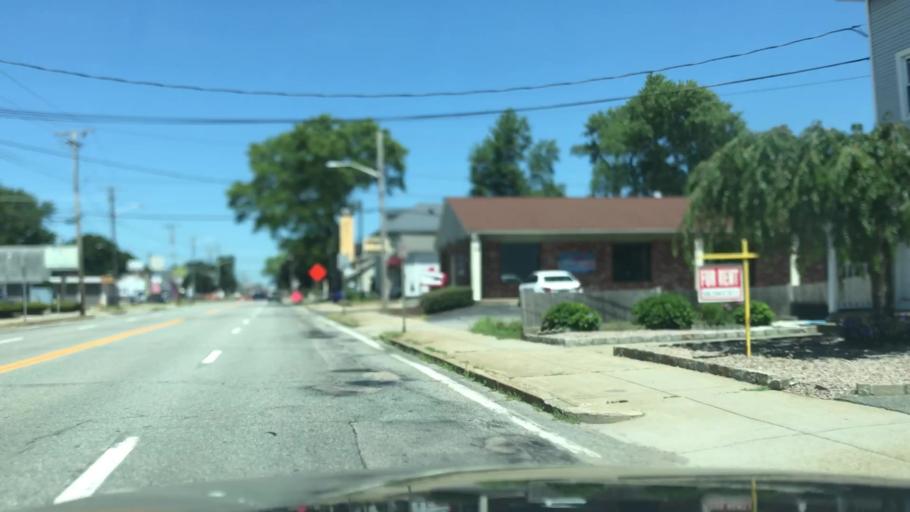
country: US
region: Rhode Island
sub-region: Providence County
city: Pawtucket
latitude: 41.8713
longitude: -71.3543
